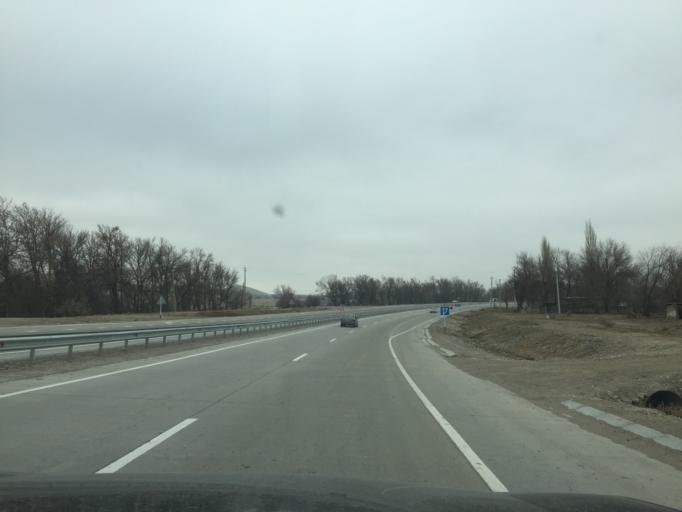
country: KZ
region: Ongtustik Qazaqstan
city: Sastobe
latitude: 42.5006
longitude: 69.9602
